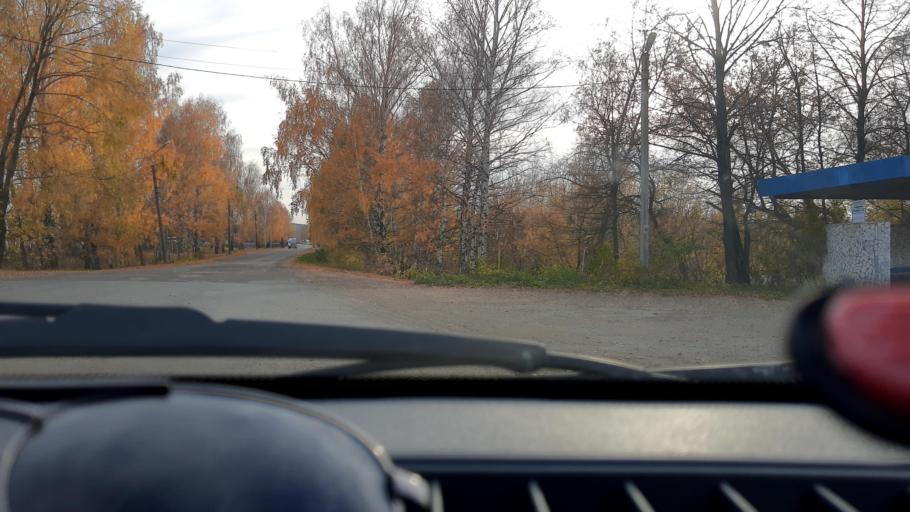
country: RU
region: Bashkortostan
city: Ufa
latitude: 54.8510
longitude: 56.1549
